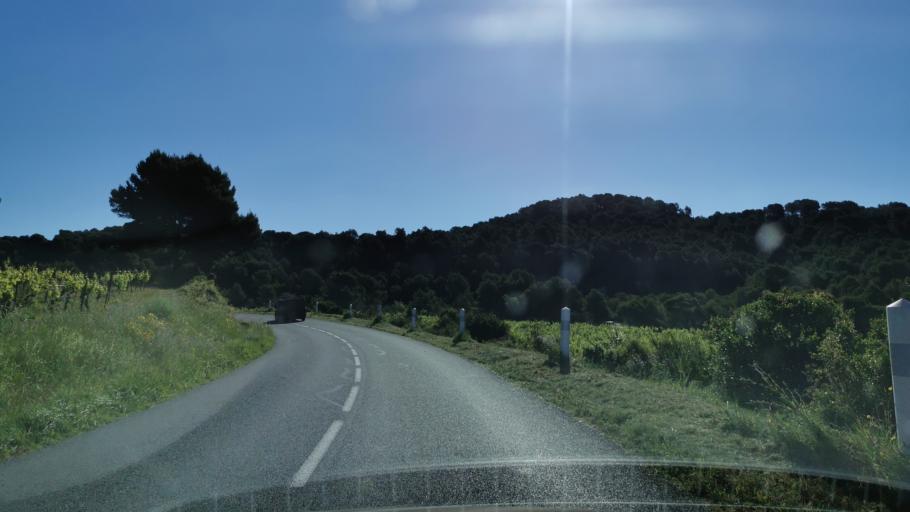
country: FR
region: Languedoc-Roussillon
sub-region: Departement de l'Aude
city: Armissan
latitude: 43.1721
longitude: 3.0750
